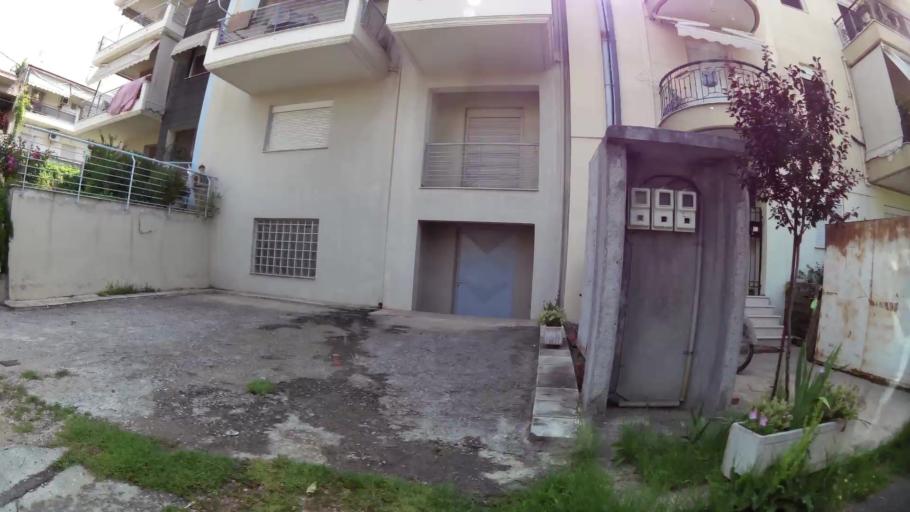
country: GR
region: Central Macedonia
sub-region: Nomos Thessalonikis
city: Stavroupoli
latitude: 40.6764
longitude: 22.9327
